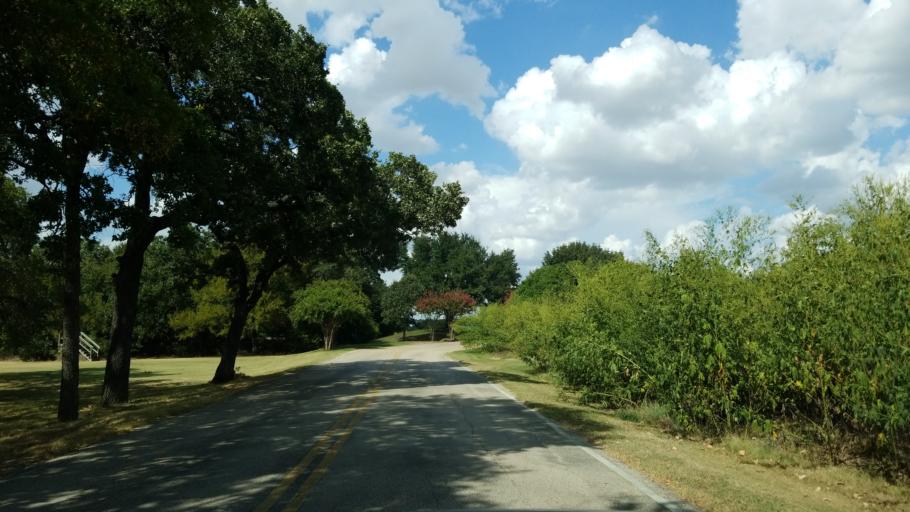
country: US
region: Texas
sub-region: Tarrant County
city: Euless
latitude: 32.8657
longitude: -97.0560
